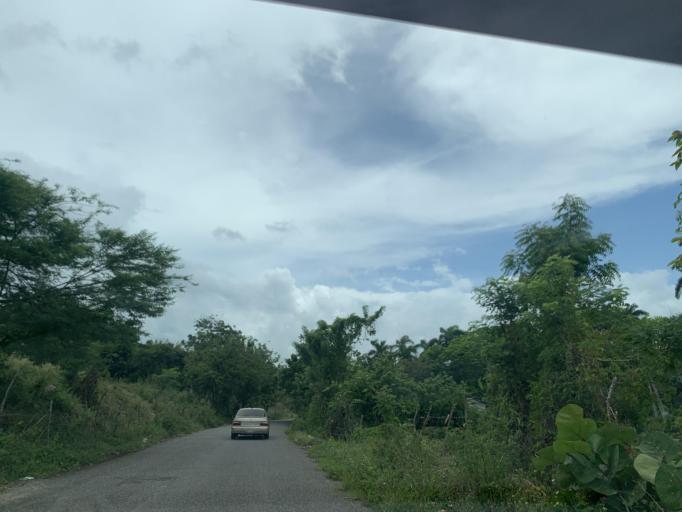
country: DO
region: Puerto Plata
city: Imbert
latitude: 19.8202
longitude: -70.7782
